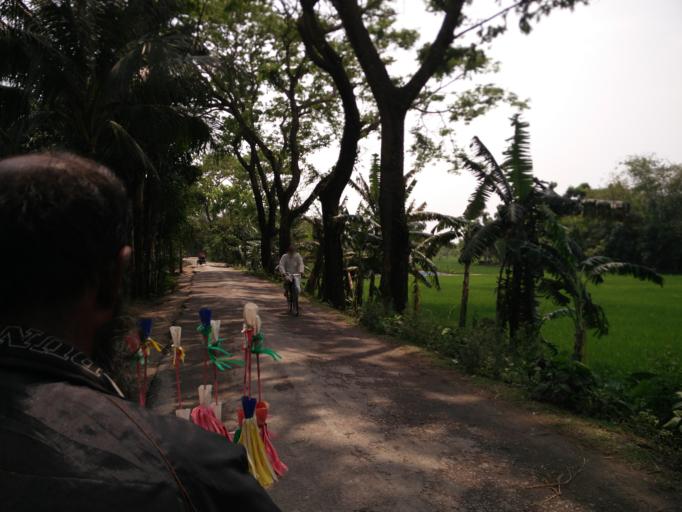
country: BD
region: Dhaka
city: Sherpur
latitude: 24.9408
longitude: 90.1599
